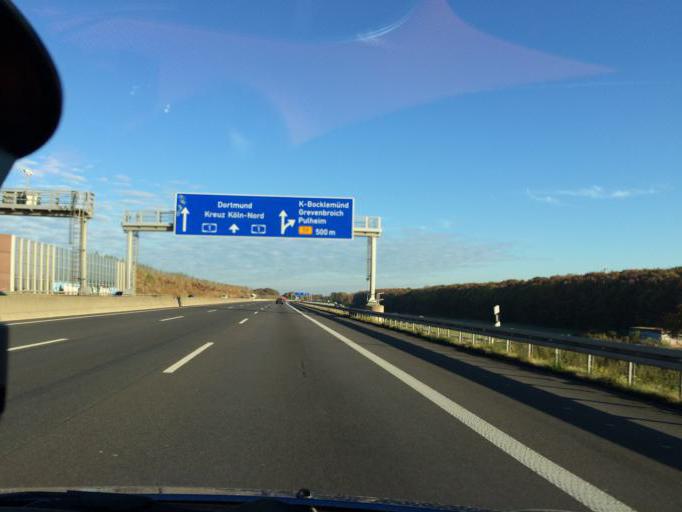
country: DE
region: North Rhine-Westphalia
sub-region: Regierungsbezirk Koln
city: Mengenich
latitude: 50.9681
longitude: 6.8505
